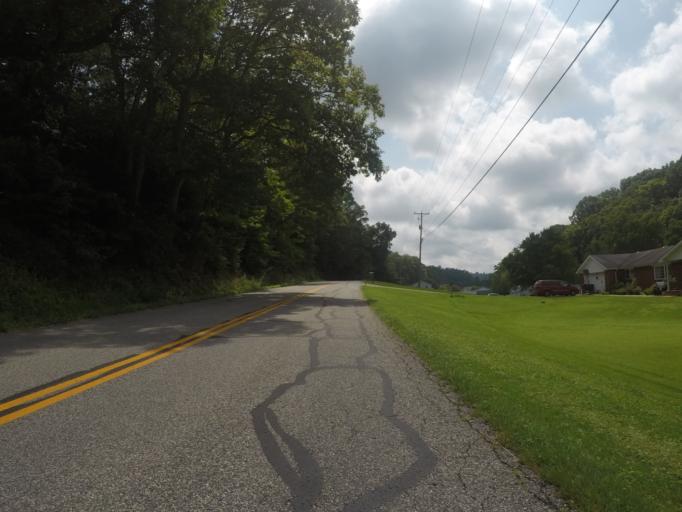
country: US
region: Kentucky
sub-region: Boyd County
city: Meads
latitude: 38.4125
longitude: -82.6756
